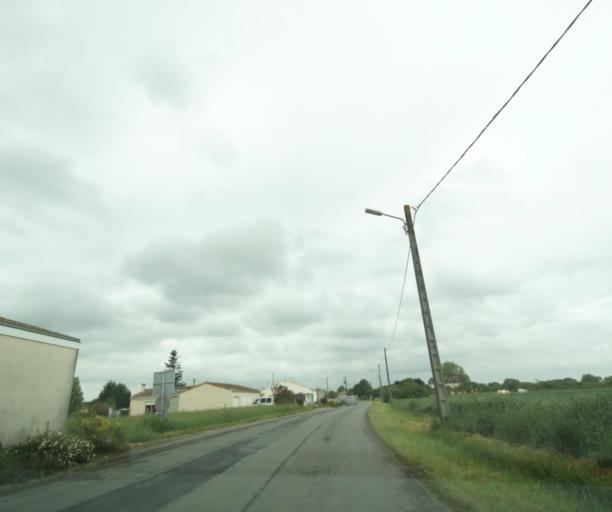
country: FR
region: Poitou-Charentes
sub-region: Departement de la Charente-Maritime
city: Chaniers
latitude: 45.6966
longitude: -0.5182
